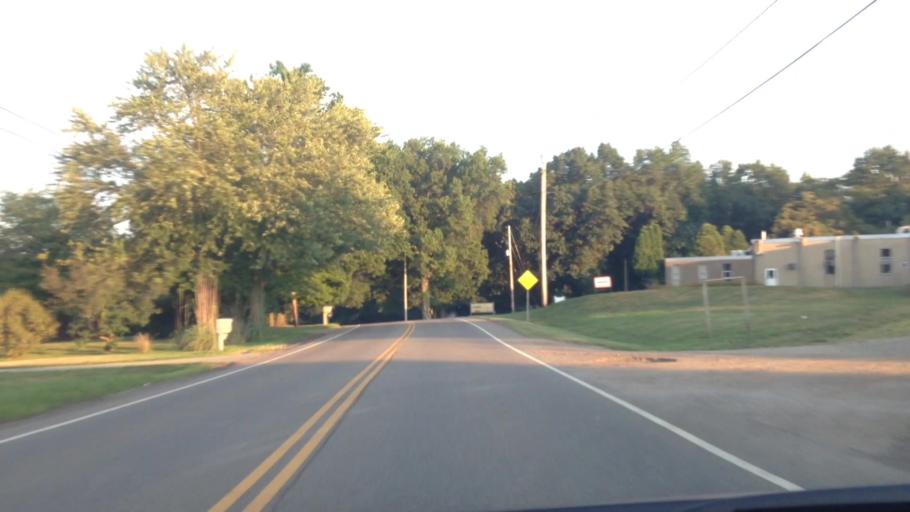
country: US
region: Ohio
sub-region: Summit County
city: Barberton
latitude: 40.9869
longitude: -81.5758
